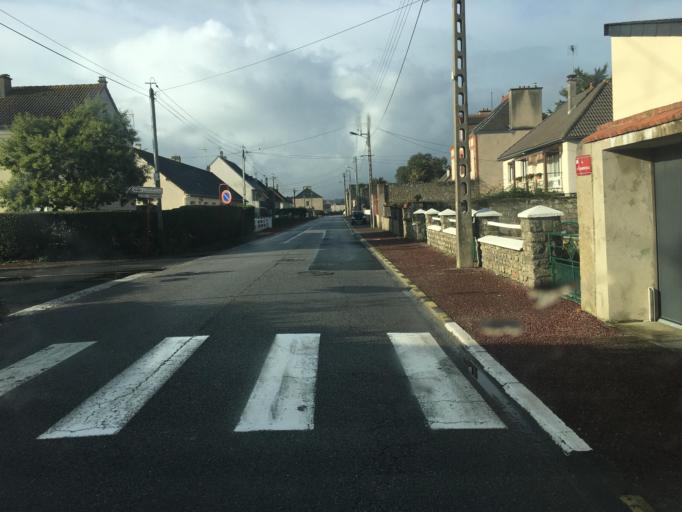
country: FR
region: Lower Normandy
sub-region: Departement de la Manche
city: Saint-Vaast-la-Hougue
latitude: 49.5853
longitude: -1.2682
